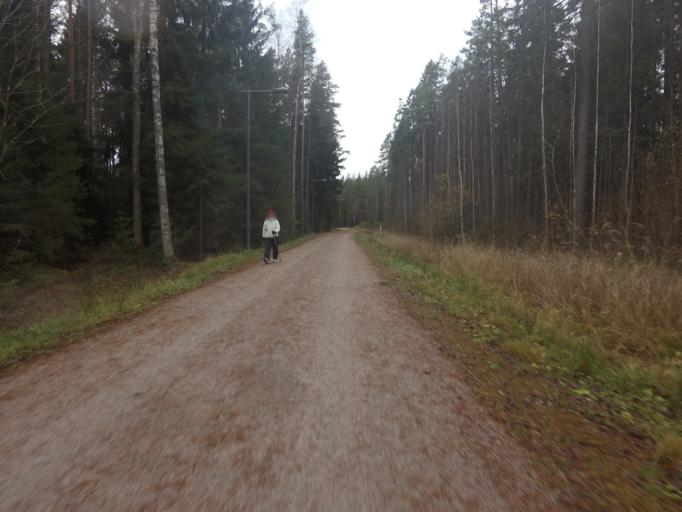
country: FI
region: Uusimaa
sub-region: Helsinki
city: Kauniainen
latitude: 60.1835
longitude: 24.6984
